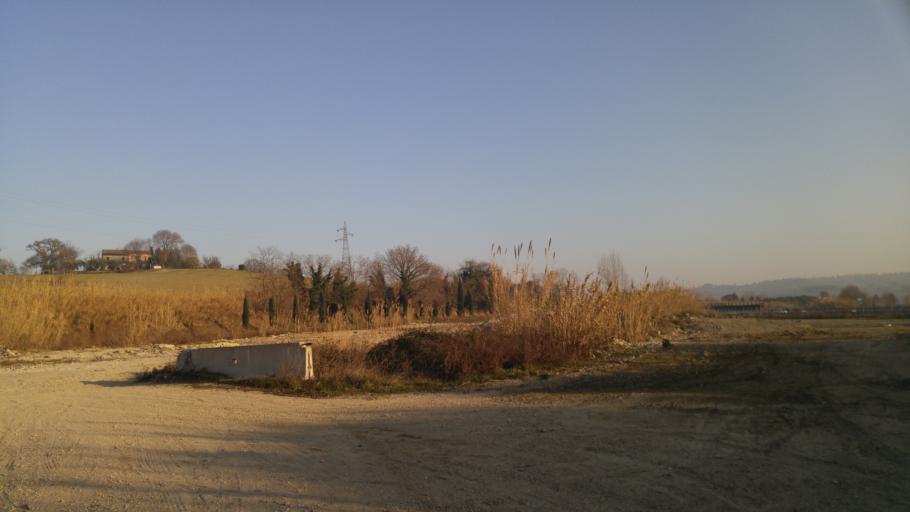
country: IT
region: The Marches
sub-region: Provincia di Pesaro e Urbino
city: Fenile
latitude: 43.8462
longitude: 12.9691
